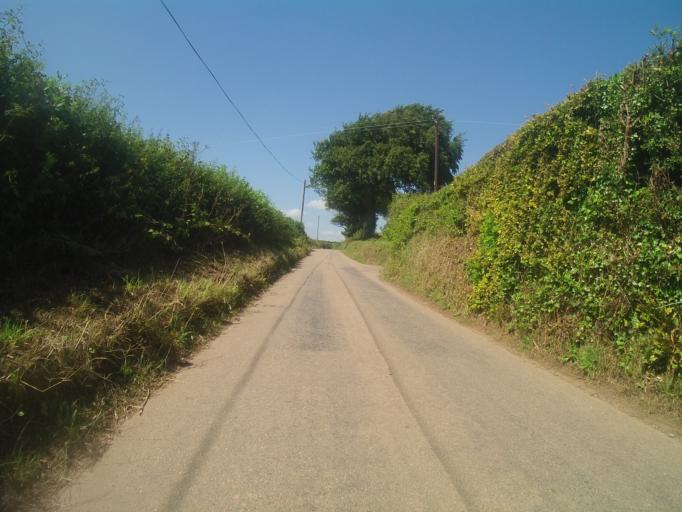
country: GB
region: England
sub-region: Devon
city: Totnes
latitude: 50.3719
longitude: -3.6536
